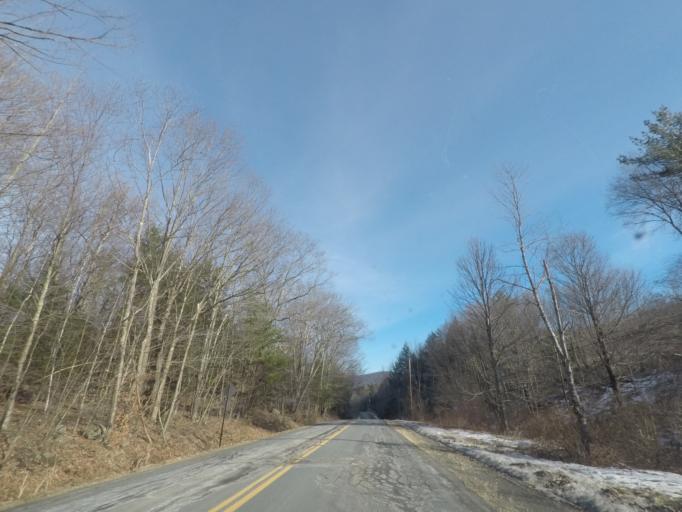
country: US
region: New York
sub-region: Rensselaer County
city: Hoosick Falls
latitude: 42.7358
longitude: -73.3762
